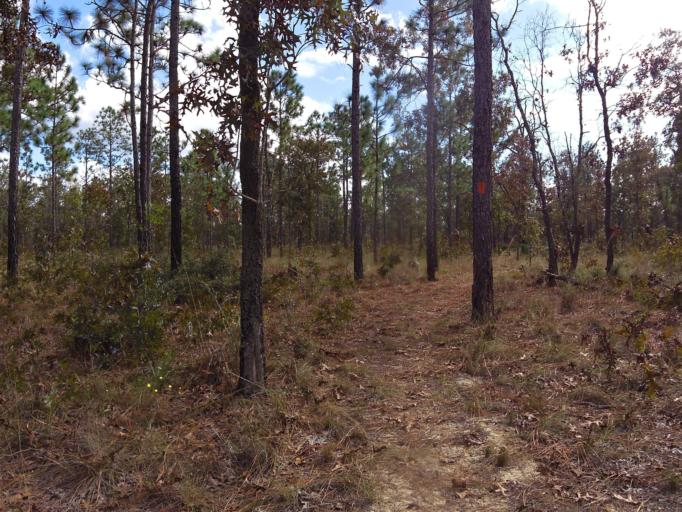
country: US
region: Florida
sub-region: Clay County
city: Keystone Heights
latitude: 29.8434
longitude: -81.9634
